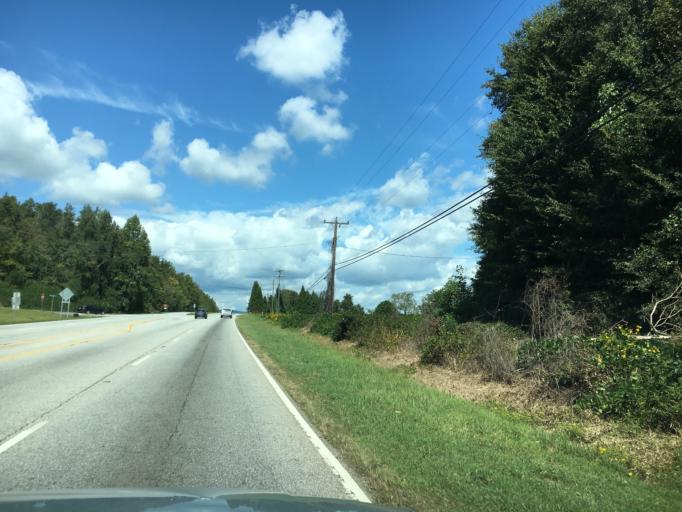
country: US
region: South Carolina
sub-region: Greenville County
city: Tigerville
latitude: 35.0329
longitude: -82.4248
